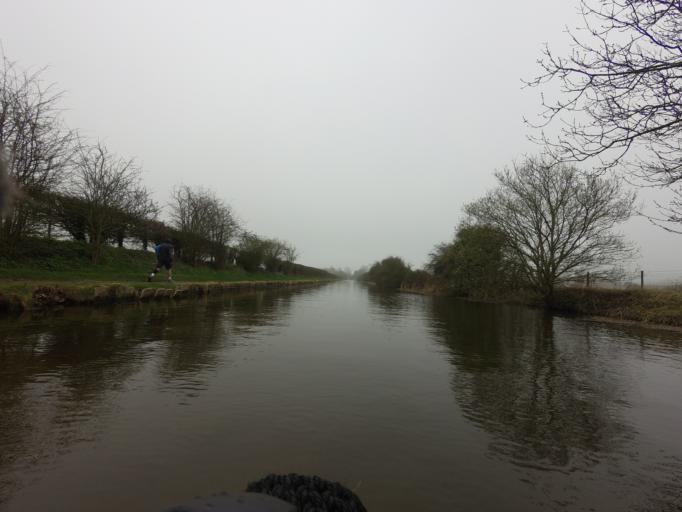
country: GB
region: England
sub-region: Hertfordshire
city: Tring
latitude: 51.7887
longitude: -0.6170
